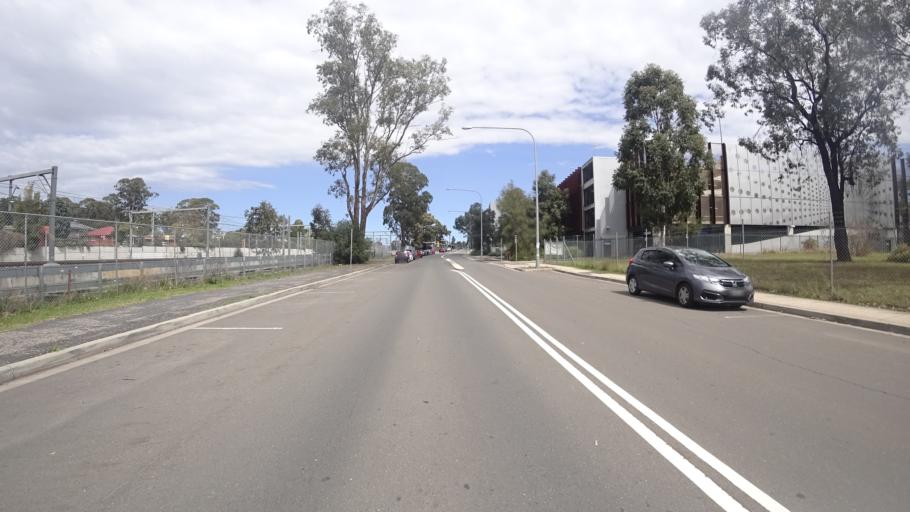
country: AU
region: New South Wales
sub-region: Campbelltown Municipality
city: Glenfield
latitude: -33.9688
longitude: 150.8963
